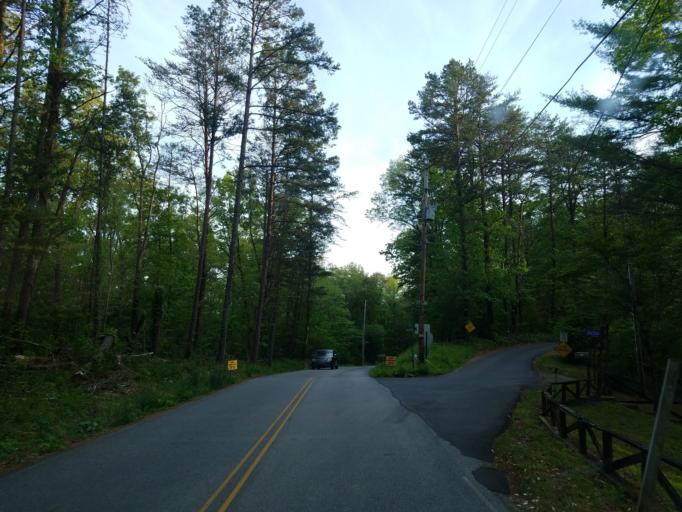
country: US
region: Georgia
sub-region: Fannin County
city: Blue Ridge
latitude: 34.8708
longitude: -84.2485
